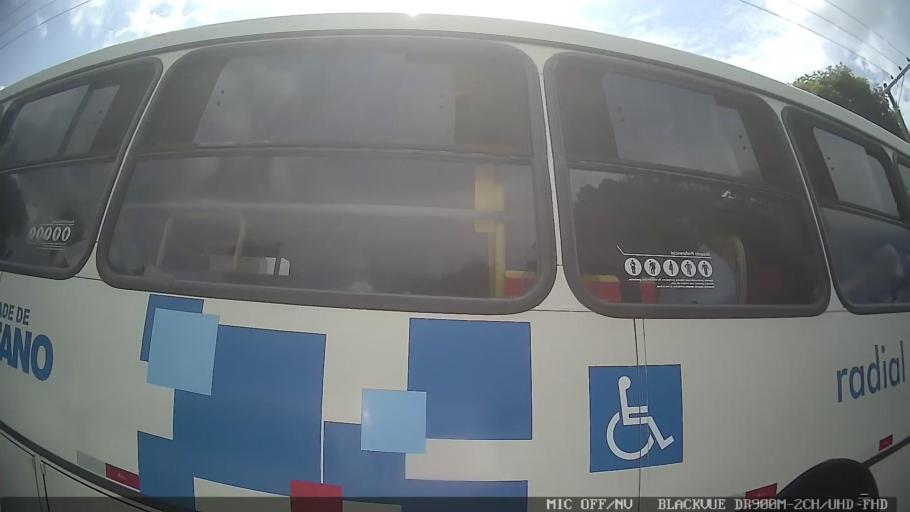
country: BR
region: Sao Paulo
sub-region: Suzano
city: Suzano
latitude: -23.5356
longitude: -46.3096
